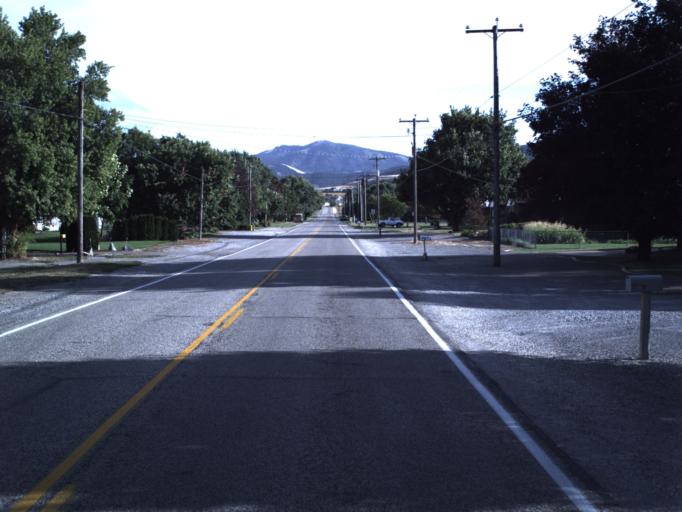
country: US
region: Utah
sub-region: Cache County
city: Wellsville
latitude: 41.6282
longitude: -111.9348
